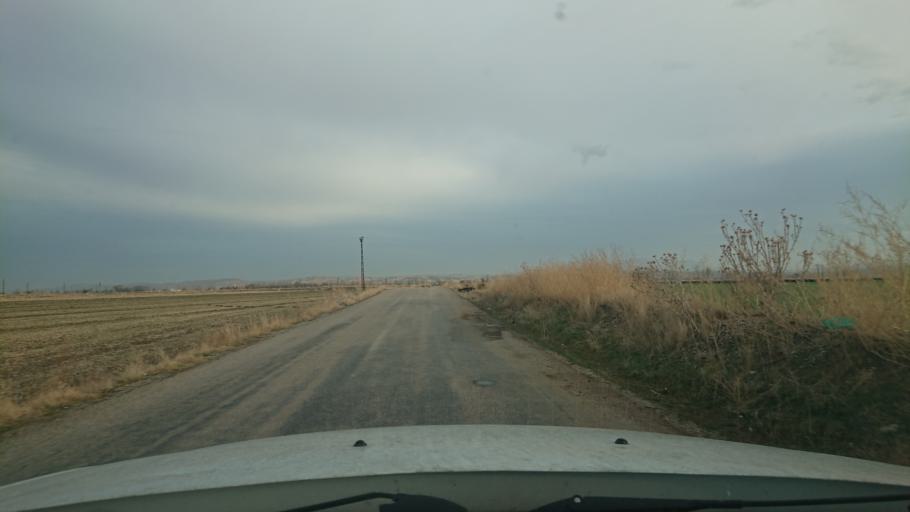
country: TR
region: Aksaray
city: Yesilova
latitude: 38.4324
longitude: 33.8365
